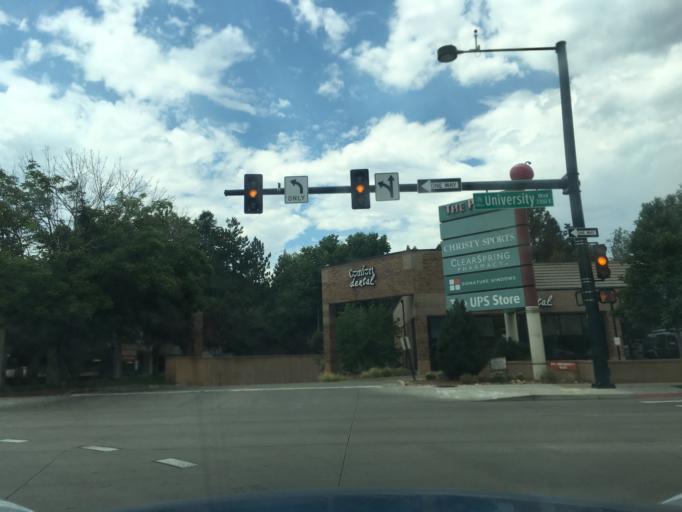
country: US
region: Colorado
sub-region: Arapahoe County
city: Glendale
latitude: 39.7196
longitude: -104.9593
